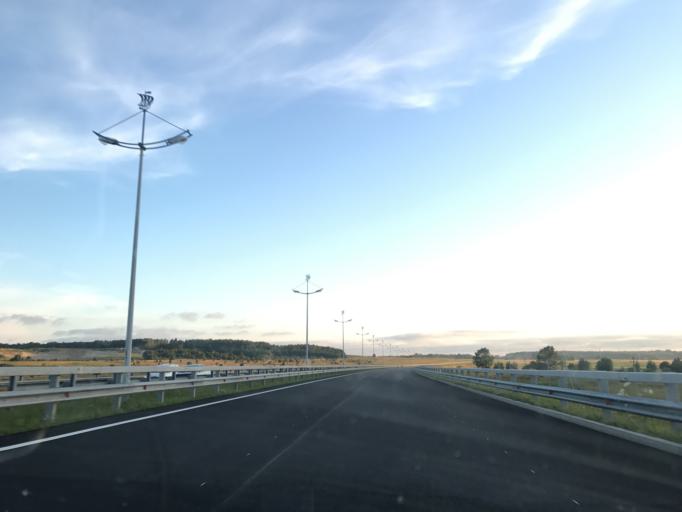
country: RU
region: Kaliningrad
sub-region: Gorod Kaliningrad
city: Pionerskiy
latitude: 54.9131
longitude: 20.2270
